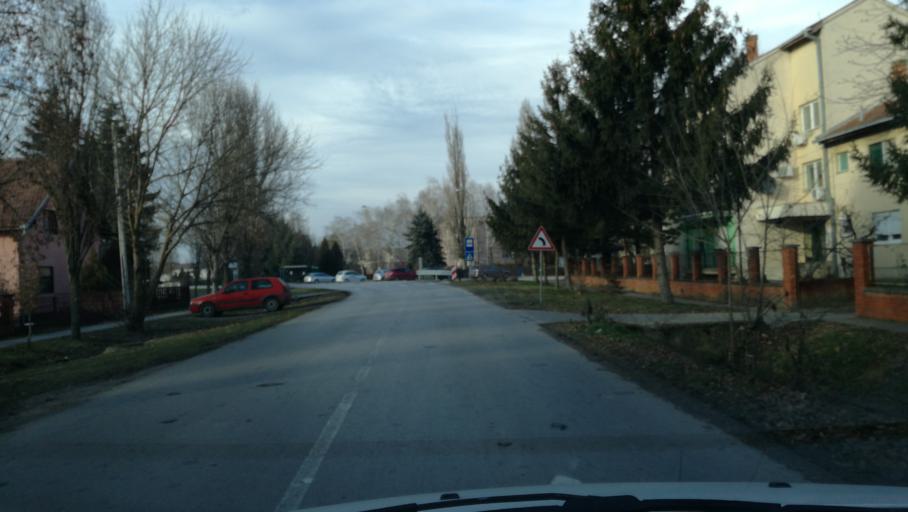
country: RS
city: Banatsko Veliko Selo
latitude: 45.8204
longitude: 20.6039
